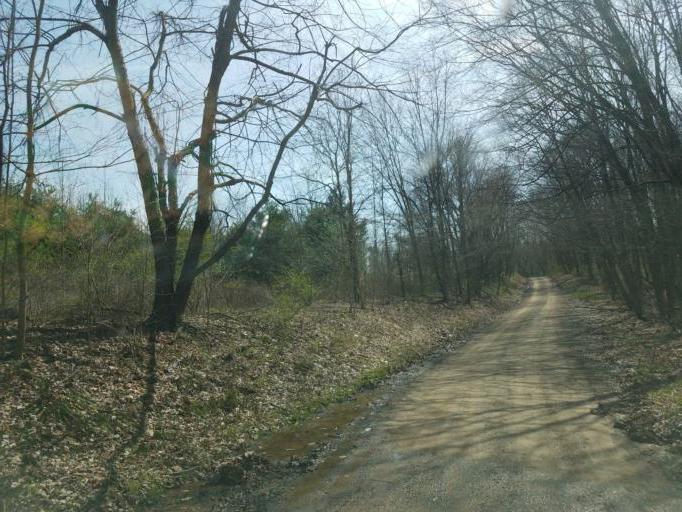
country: US
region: Ohio
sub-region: Knox County
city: Oak Hill
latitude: 40.3817
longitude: -82.1637
